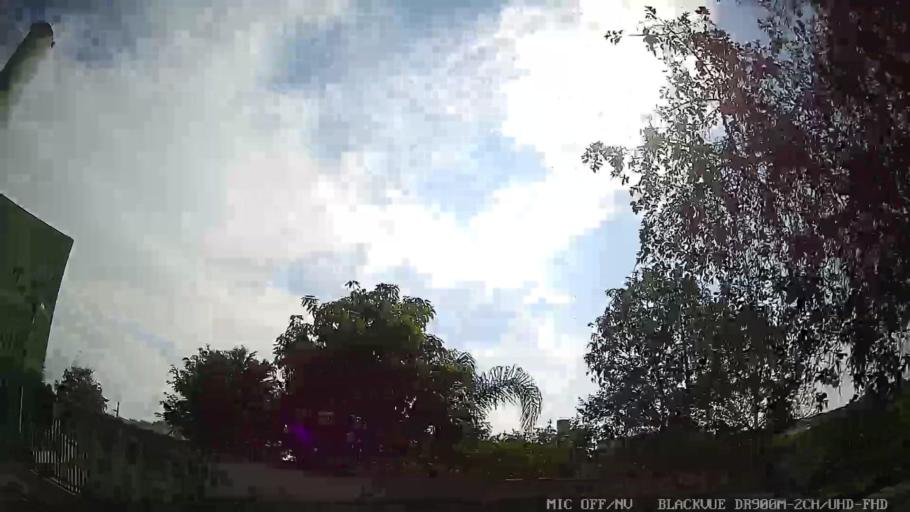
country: BR
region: Sao Paulo
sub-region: Ferraz De Vasconcelos
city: Ferraz de Vasconcelos
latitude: -23.5097
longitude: -46.4173
